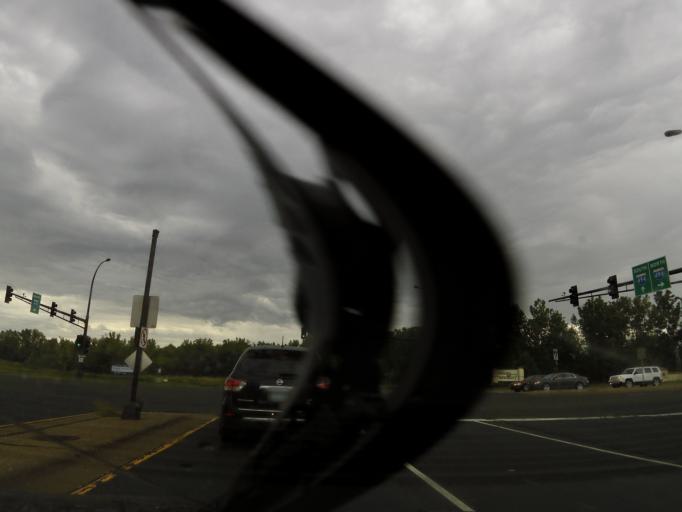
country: US
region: Minnesota
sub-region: Washington County
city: Woodbury
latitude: 44.9368
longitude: -92.9579
